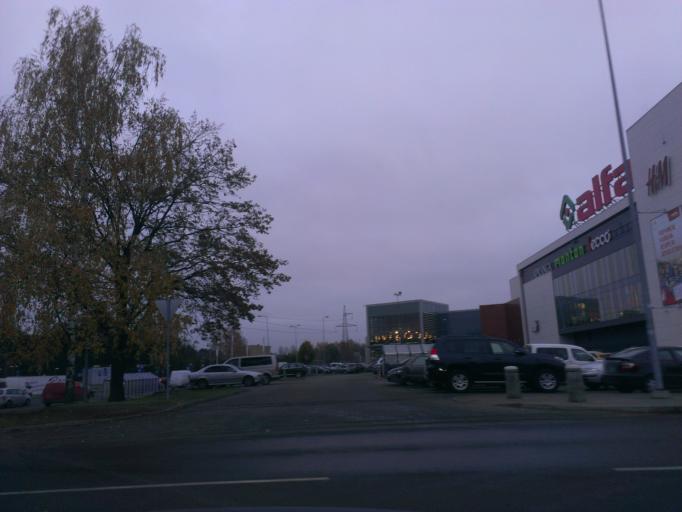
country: LV
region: Riga
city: Jaunciems
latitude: 56.9838
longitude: 24.2047
